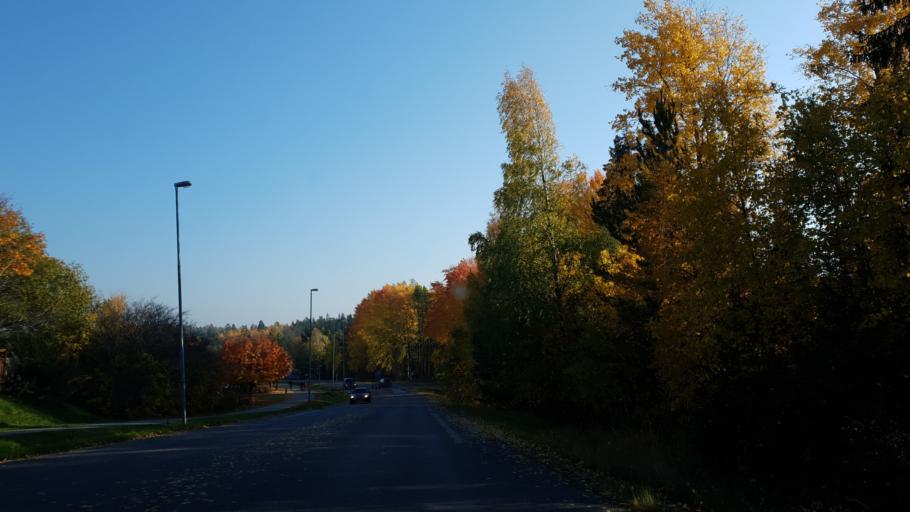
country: SE
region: Stockholm
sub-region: Haninge Kommun
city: Haninge
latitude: 59.1706
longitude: 18.1928
